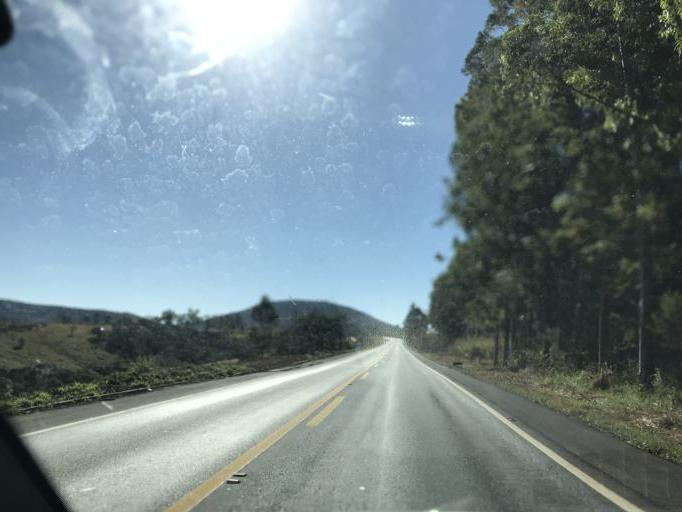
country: BR
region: Minas Gerais
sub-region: Campos Altos
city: Campos Altos
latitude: -19.8165
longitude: -46.0287
